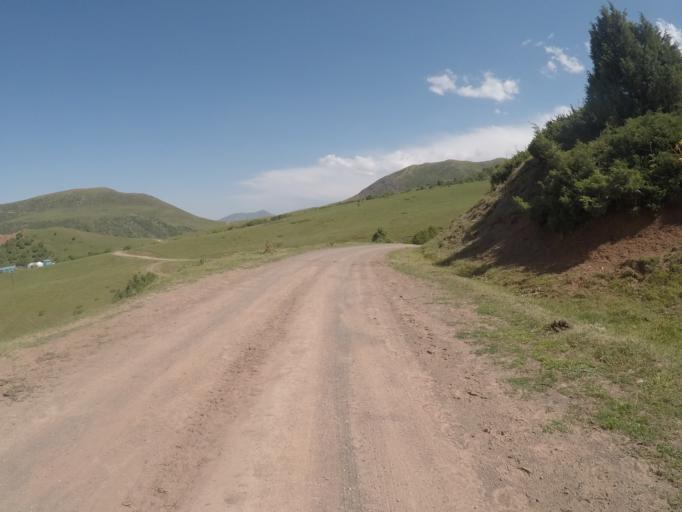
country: KG
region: Chuy
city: Bishkek
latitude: 42.6466
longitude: 74.5617
